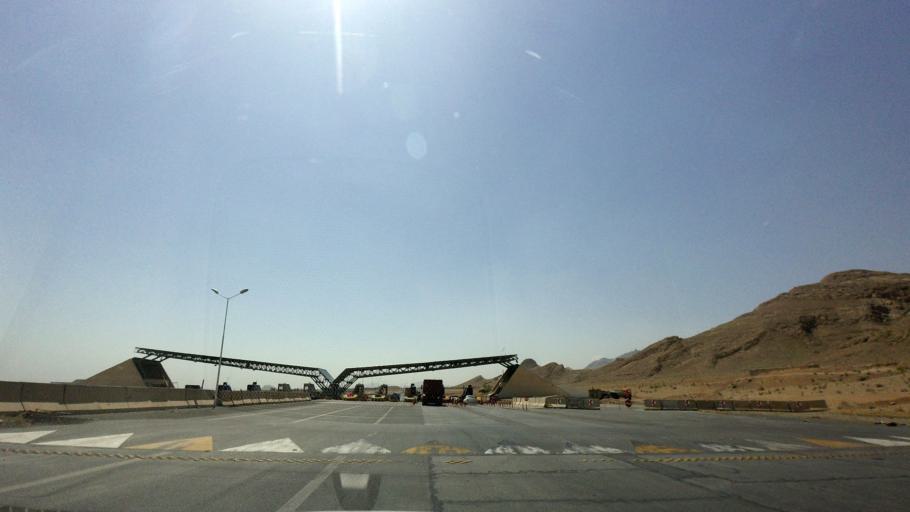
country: IR
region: Isfahan
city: Najafabad
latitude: 32.5829
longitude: 51.2875
